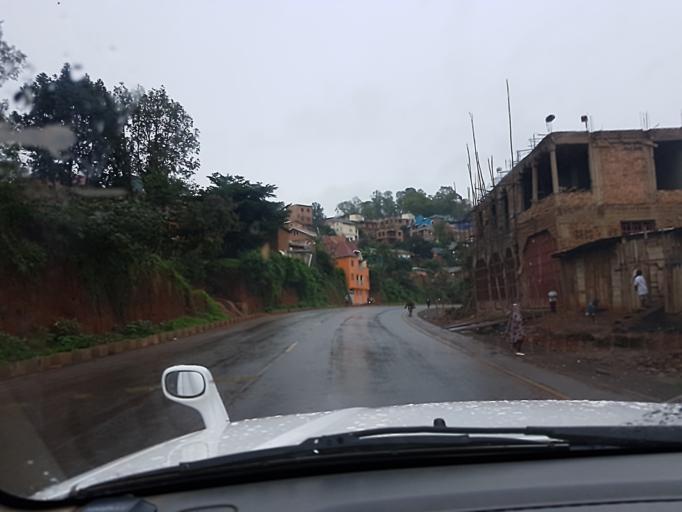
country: CD
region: South Kivu
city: Bukavu
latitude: -2.5086
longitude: 28.8555
